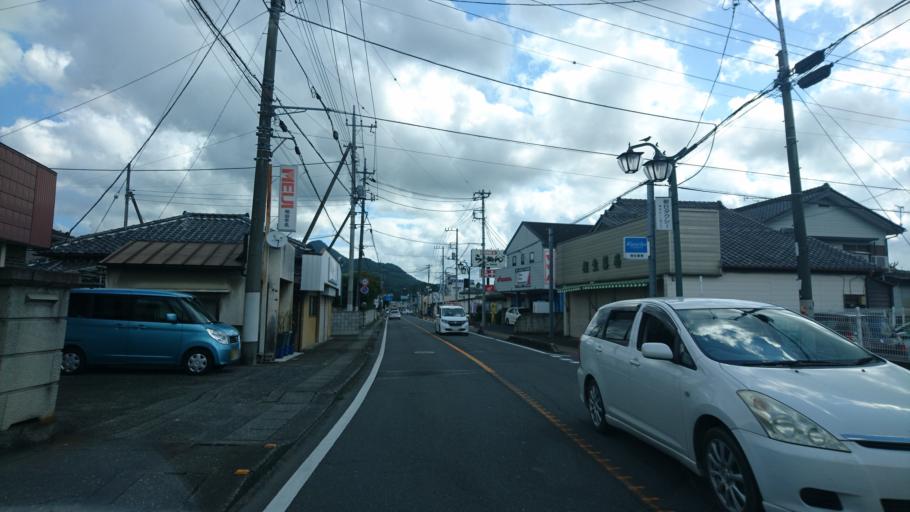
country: JP
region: Gunma
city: Kiryu
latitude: 36.4097
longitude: 139.3065
